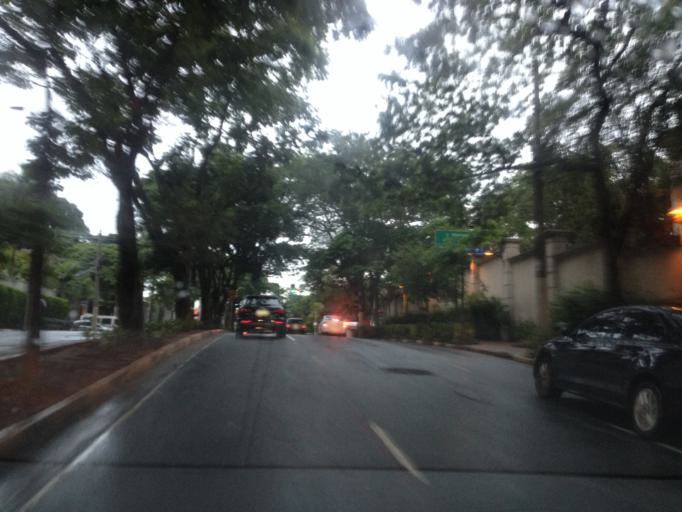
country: BR
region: Sao Paulo
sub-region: Sao Paulo
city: Sao Paulo
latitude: -23.5968
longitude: -46.6641
